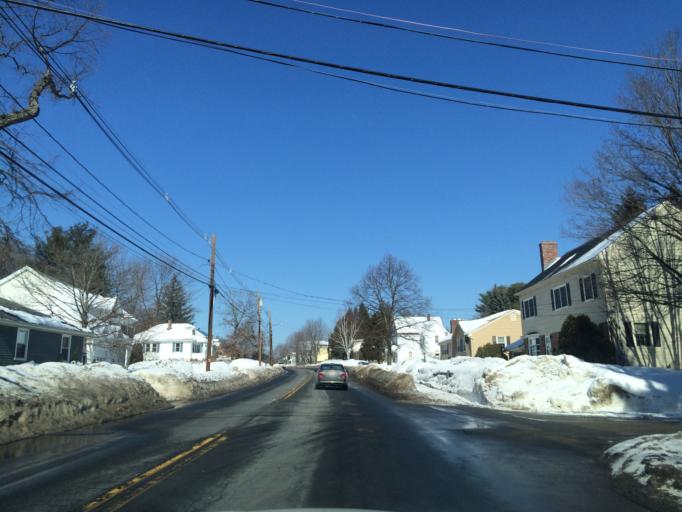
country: US
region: Massachusetts
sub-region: Norfolk County
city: Needham
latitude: 42.2958
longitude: -71.2464
